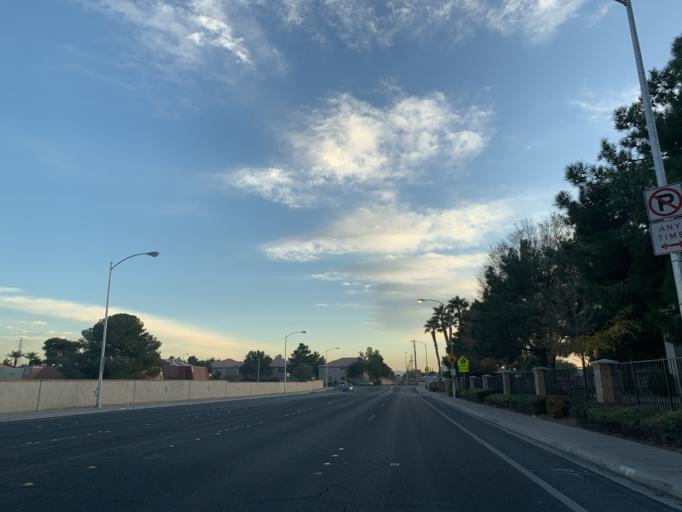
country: US
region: Nevada
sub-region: Clark County
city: Spring Valley
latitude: 36.1091
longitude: -115.2166
